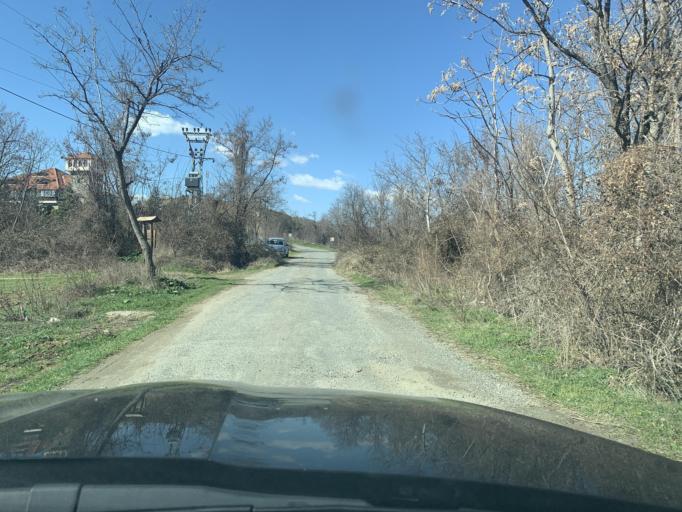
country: MK
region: Demir Kapija
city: Demir Kapija
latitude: 41.4103
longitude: 22.2281
